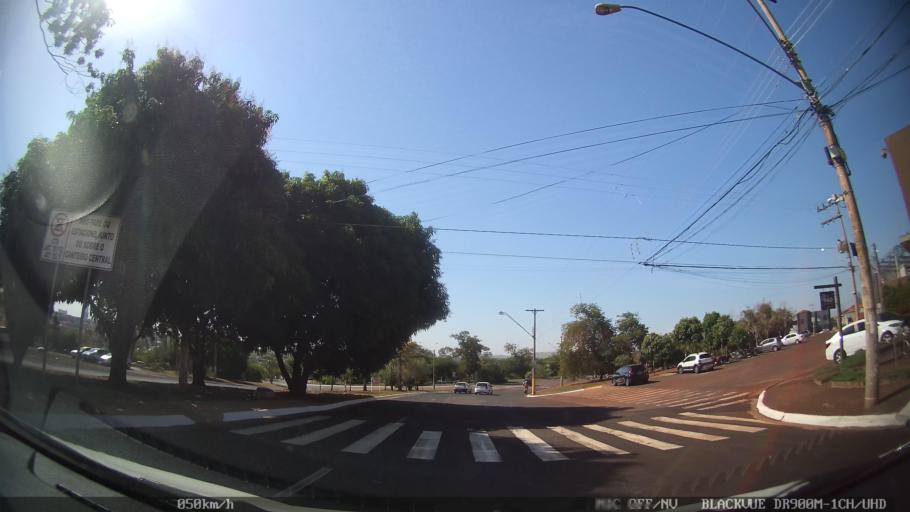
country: BR
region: Sao Paulo
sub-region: Ribeirao Preto
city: Ribeirao Preto
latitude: -21.2159
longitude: -47.7824
